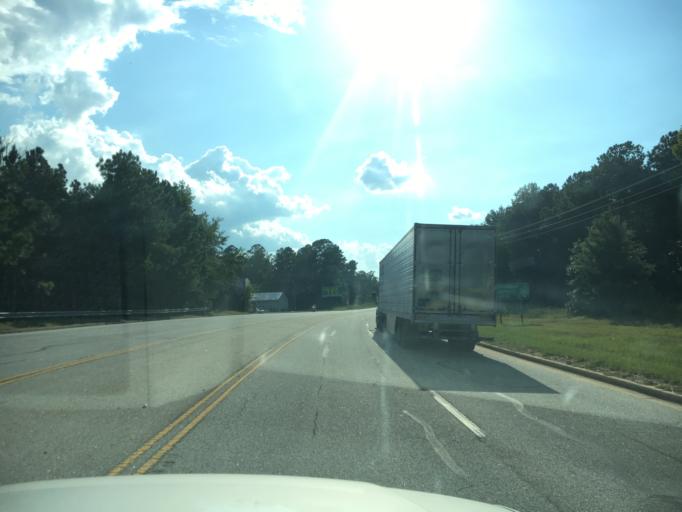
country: US
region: South Carolina
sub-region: Greenwood County
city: Ninety Six
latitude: 34.2874
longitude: -82.0447
